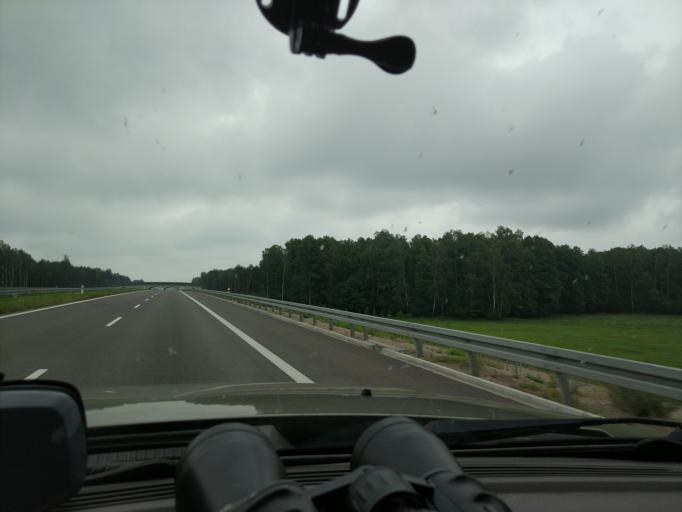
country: PL
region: Podlasie
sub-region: Powiat zambrowski
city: Zambrow
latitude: 53.0229
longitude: 22.3218
